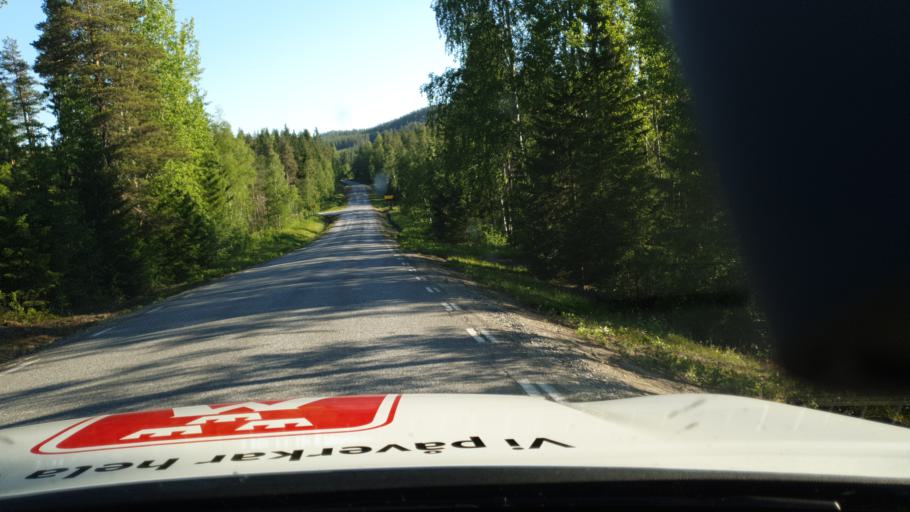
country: SE
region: Vaesterbotten
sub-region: Vannas Kommun
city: Vannasby
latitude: 64.0673
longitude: 20.0648
